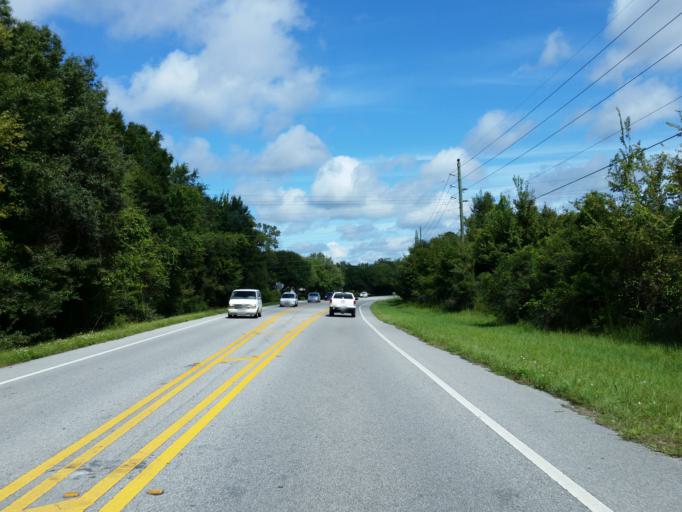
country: US
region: Florida
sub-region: Pasco County
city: Land O' Lakes
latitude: 28.1986
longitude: -82.3991
